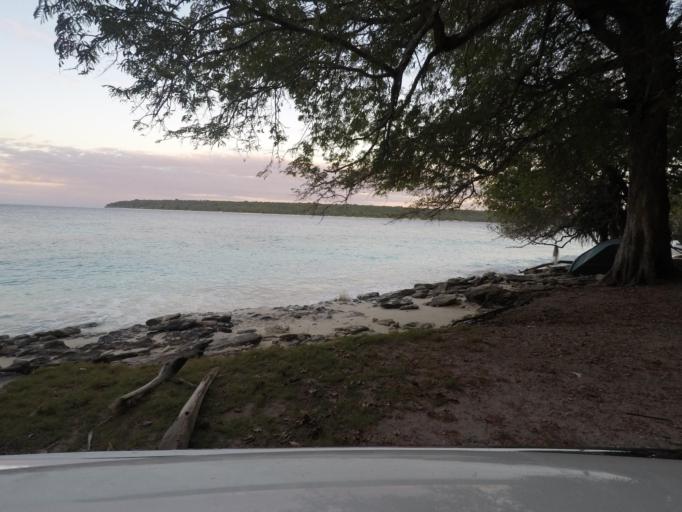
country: TL
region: Lautem
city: Lospalos
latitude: -8.4150
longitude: 127.3008
